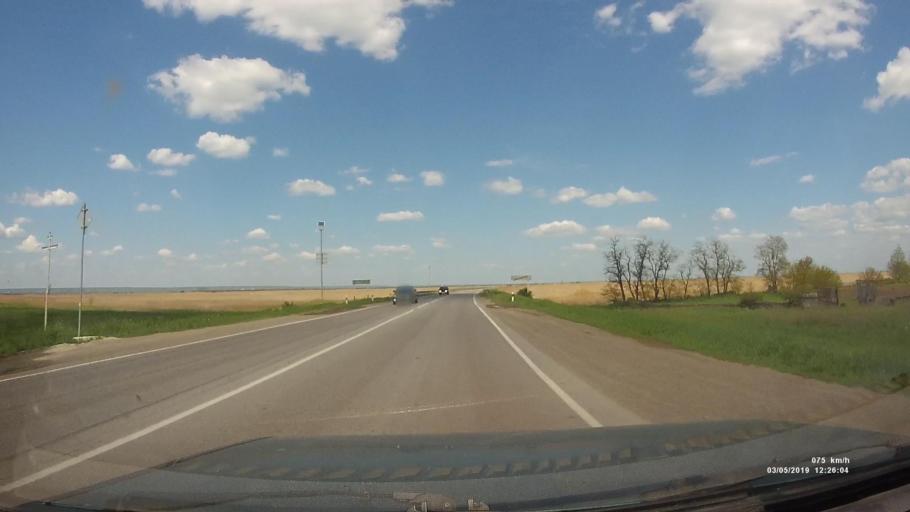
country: RU
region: Rostov
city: Semikarakorsk
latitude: 47.4404
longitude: 40.7121
